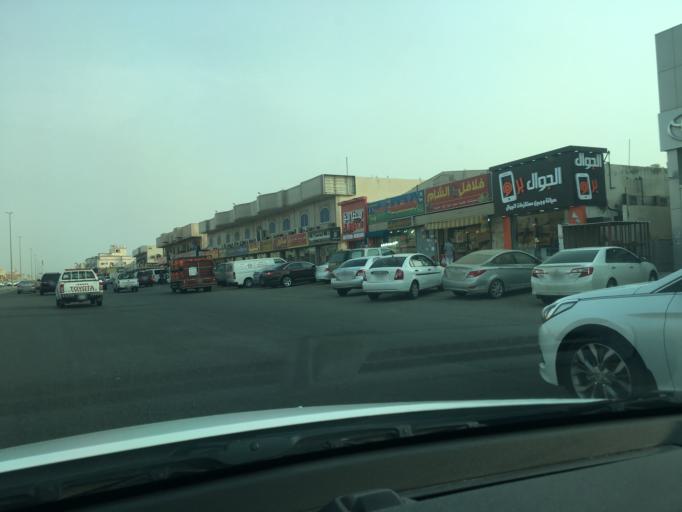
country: SA
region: Makkah
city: Jeddah
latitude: 21.7553
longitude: 39.1858
